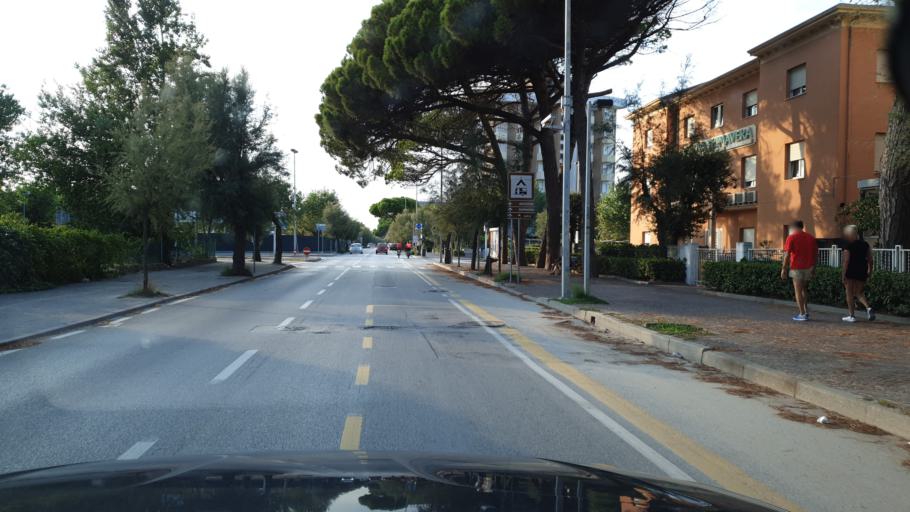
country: IT
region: Emilia-Romagna
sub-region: Provincia di Rimini
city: Misano Adriatico
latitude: 43.9884
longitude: 12.6837
